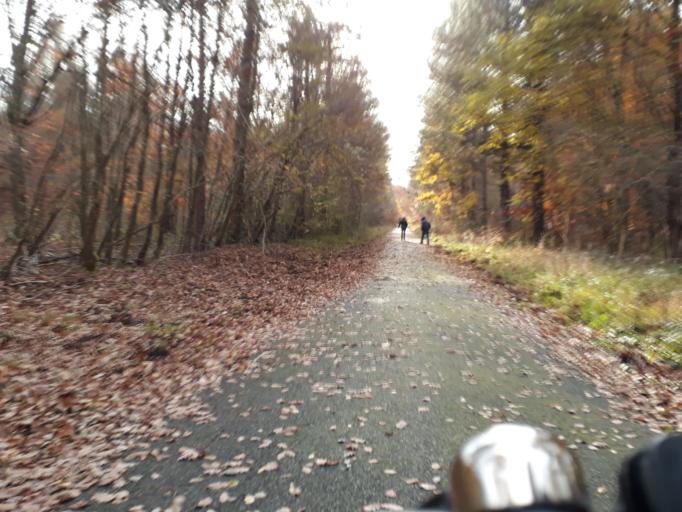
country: FR
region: Ile-de-France
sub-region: Departement de Seine-et-Marne
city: Bois-le-Roi
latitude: 48.4634
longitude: 2.6863
